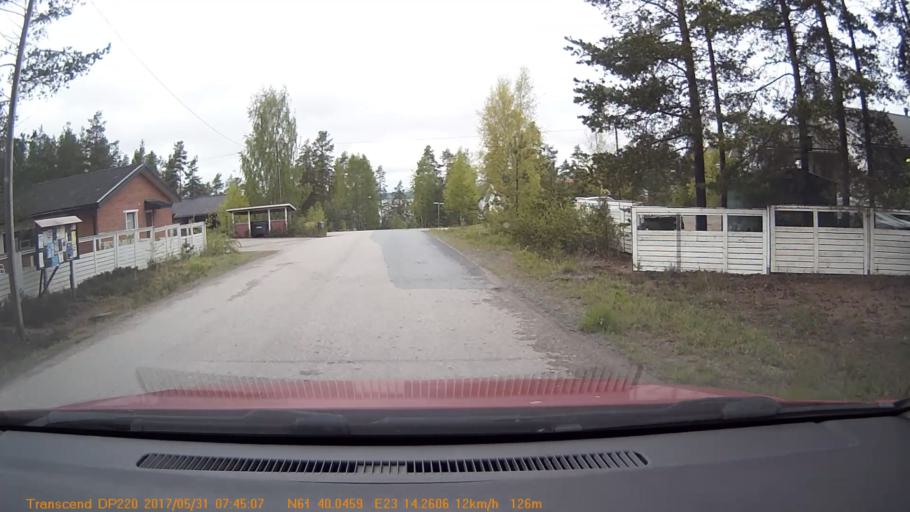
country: FI
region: Pirkanmaa
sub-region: Tampere
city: Viljakkala
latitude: 61.6675
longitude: 23.2376
